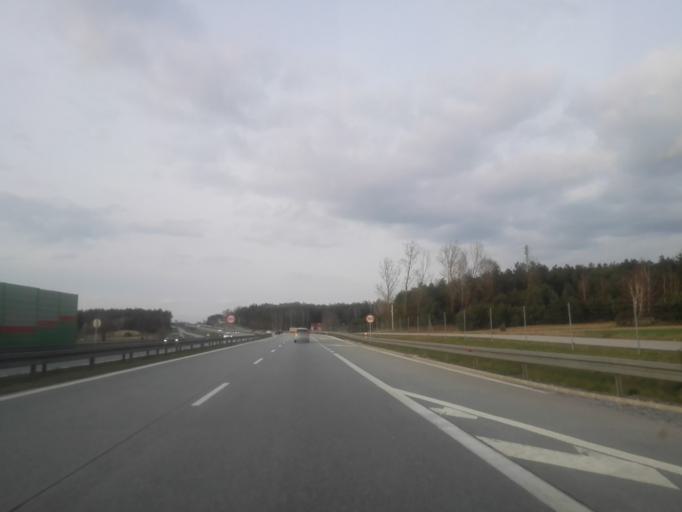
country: PL
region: Lodz Voivodeship
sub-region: Powiat tomaszowski
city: Czerniewice
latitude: 51.6944
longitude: 20.2133
